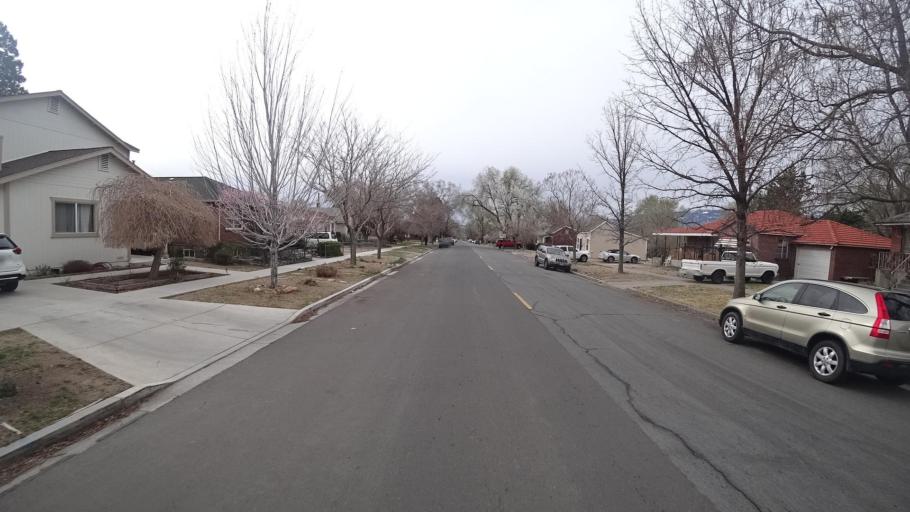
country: US
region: Nevada
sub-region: Washoe County
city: Reno
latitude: 39.5371
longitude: -119.8262
